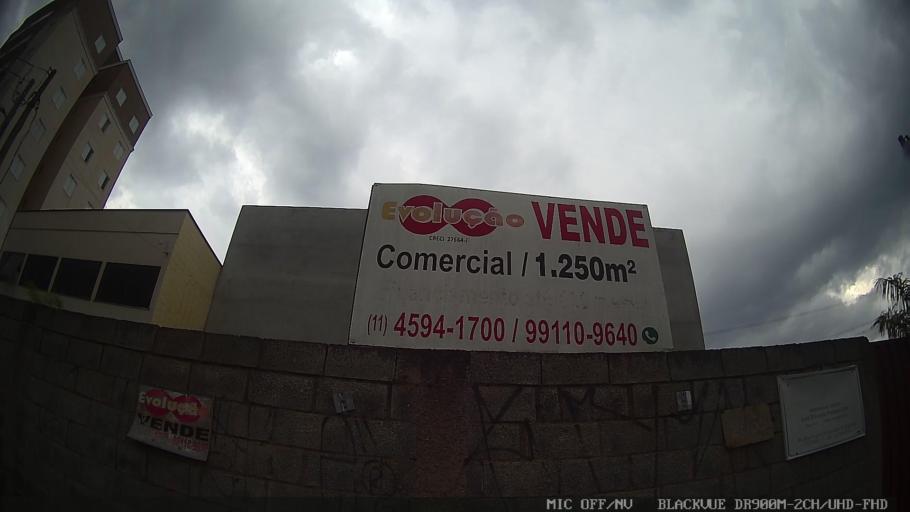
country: BR
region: Sao Paulo
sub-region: Itatiba
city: Itatiba
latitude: -23.0094
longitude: -46.8670
